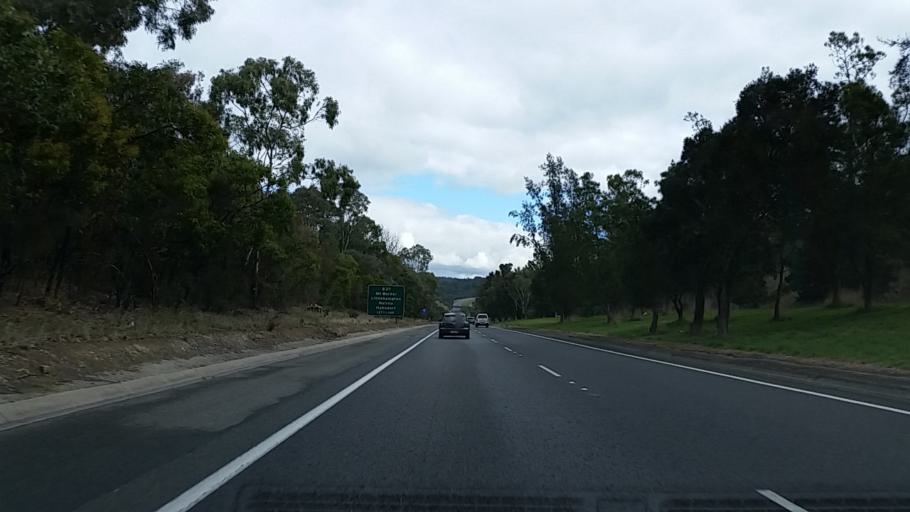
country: AU
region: South Australia
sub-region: Mount Barker
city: Mount Barker
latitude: -35.0551
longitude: 138.8647
